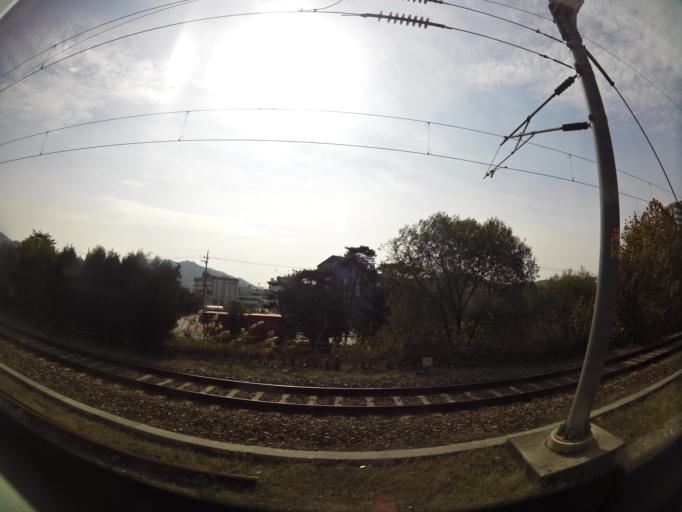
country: KR
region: Daejeon
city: Sintansin
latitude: 36.5318
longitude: 127.3682
